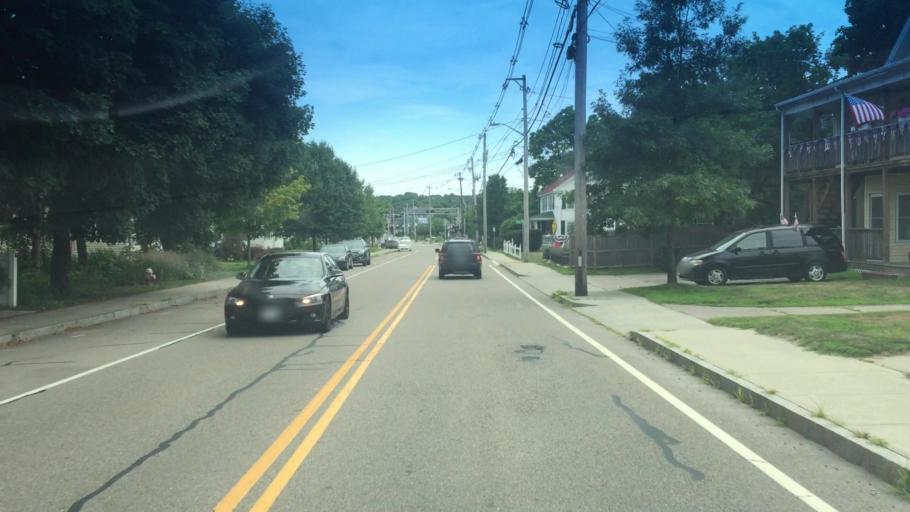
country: US
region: Massachusetts
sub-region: Norfolk County
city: Franklin
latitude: 42.0800
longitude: -71.4035
